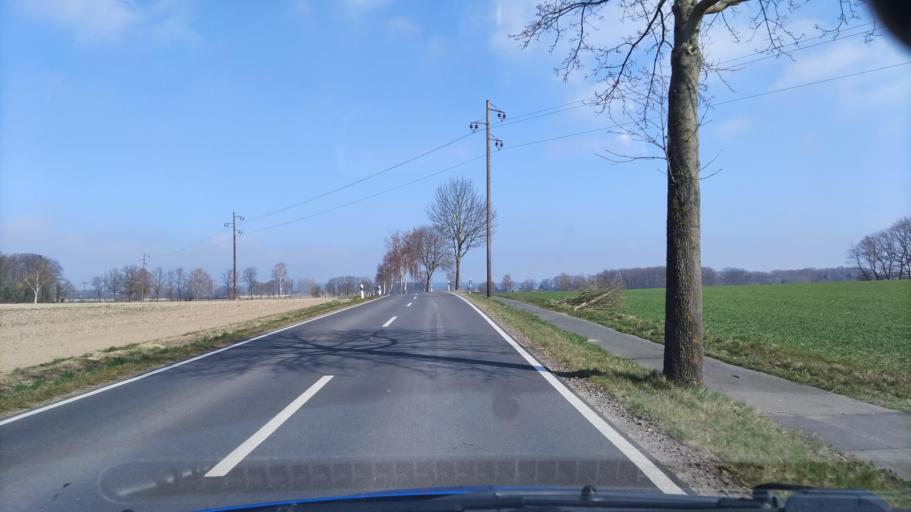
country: DE
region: Lower Saxony
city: Waddeweitz
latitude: 52.9730
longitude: 10.9719
